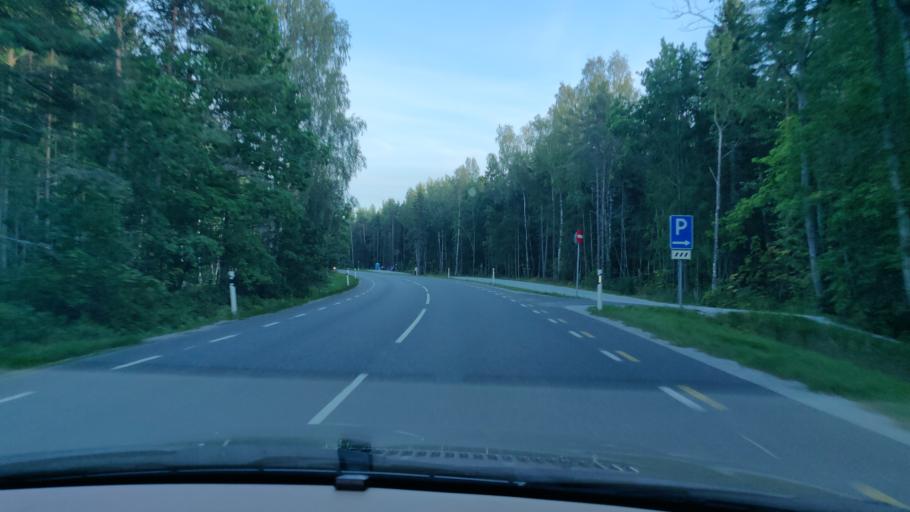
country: EE
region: Harju
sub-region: Keila linn
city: Keila
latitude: 59.3685
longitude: 24.2457
